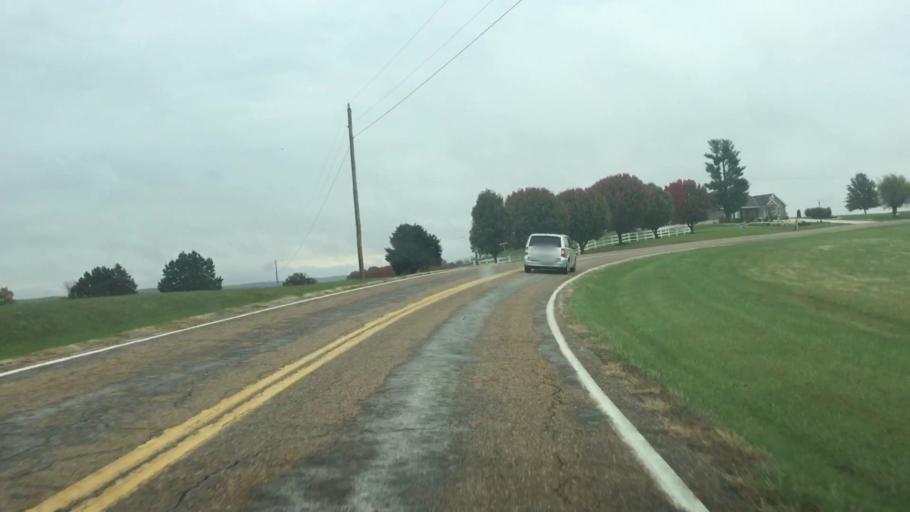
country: US
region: Missouri
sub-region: Callaway County
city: Fulton
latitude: 38.7407
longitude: -91.7068
